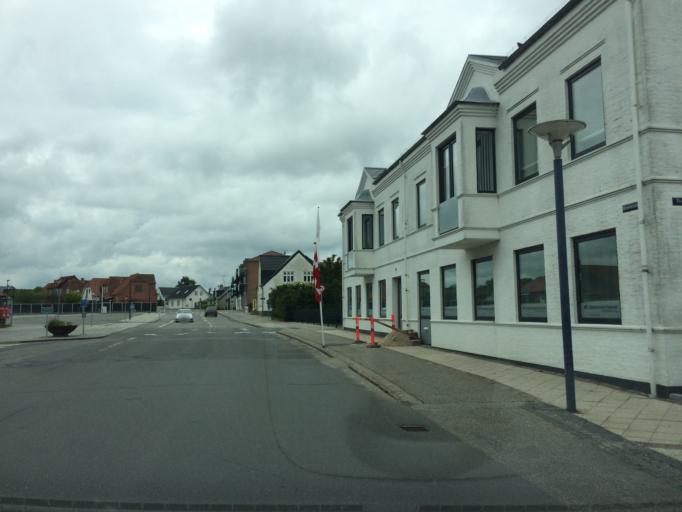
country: DK
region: North Denmark
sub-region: Vesthimmerland Kommune
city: Aars
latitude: 56.8035
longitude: 9.5125
